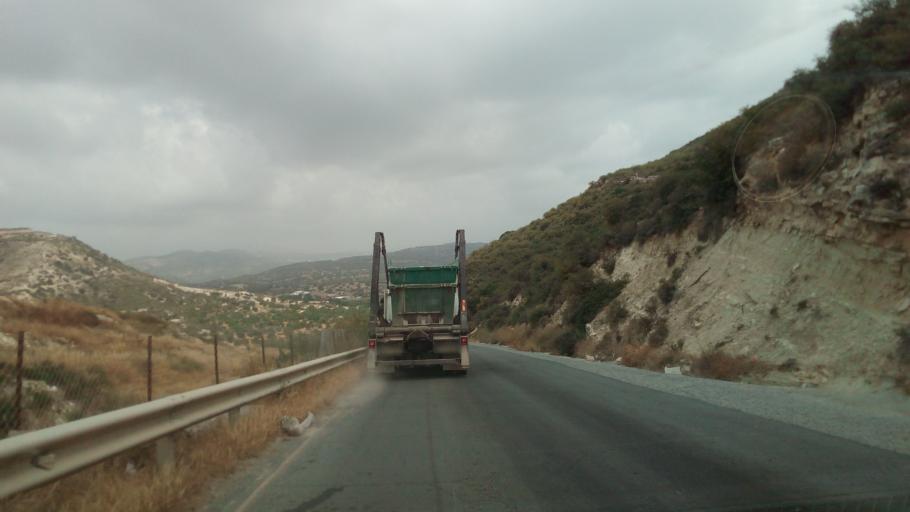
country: CY
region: Limassol
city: Pano Polemidia
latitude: 34.7500
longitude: 32.9536
